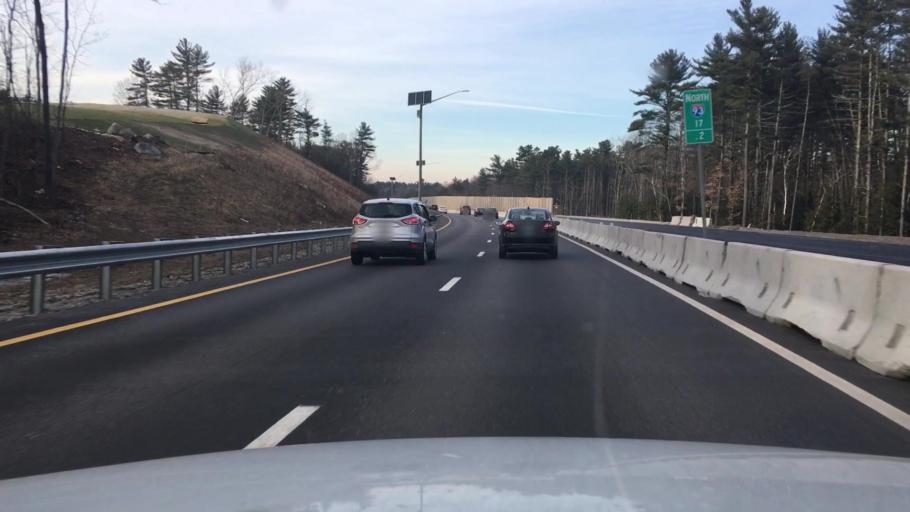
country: US
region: New Hampshire
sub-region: Rockingham County
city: Auburn
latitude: 42.9416
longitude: -71.3864
